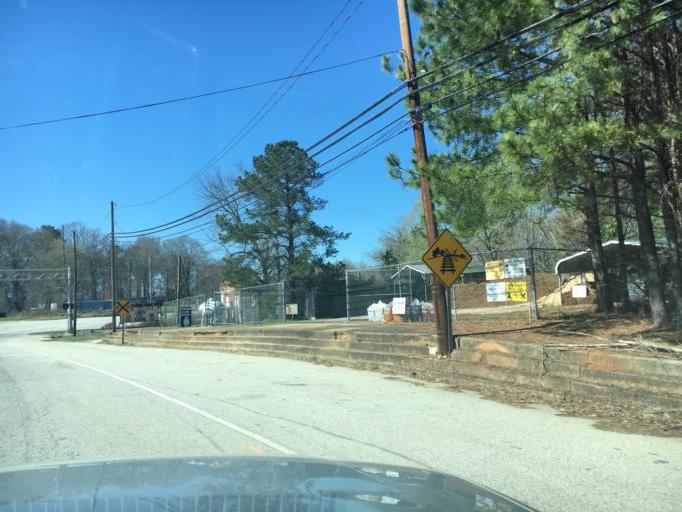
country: US
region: South Carolina
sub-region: Greenwood County
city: Ninety Six
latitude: 34.3048
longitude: -81.9828
